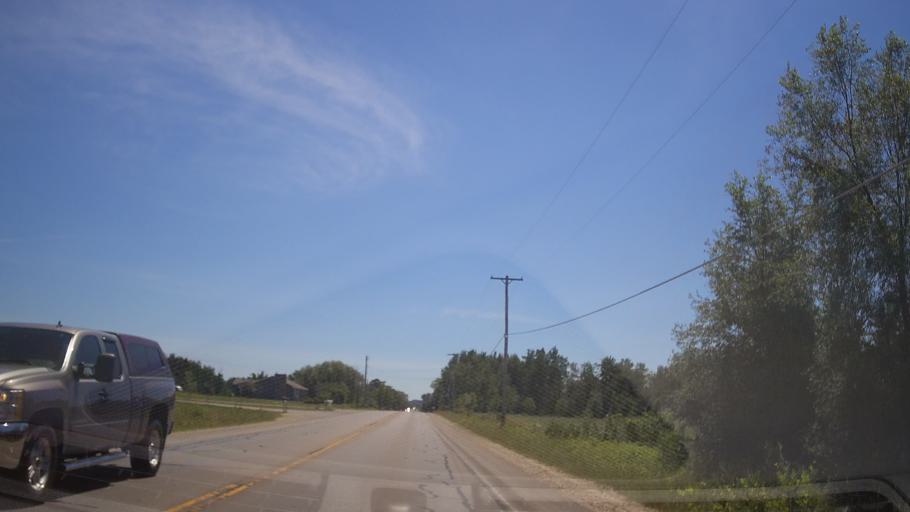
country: US
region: Michigan
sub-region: Grand Traverse County
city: Traverse City
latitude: 44.6829
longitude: -85.6896
